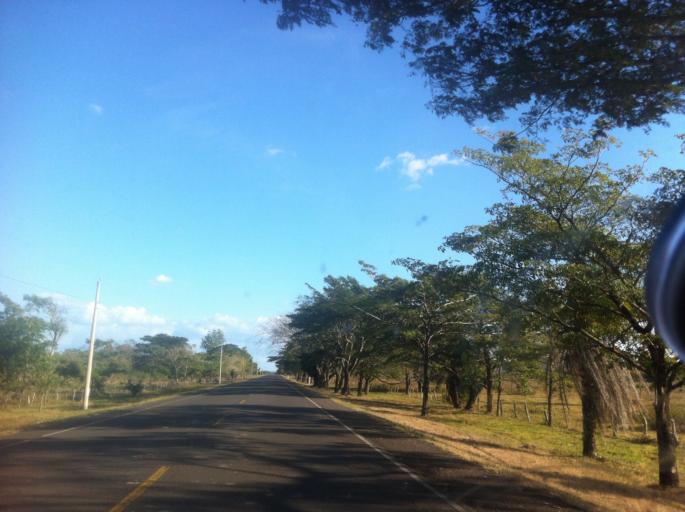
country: NI
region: Rio San Juan
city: Morrito
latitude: 11.7752
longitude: -85.0155
